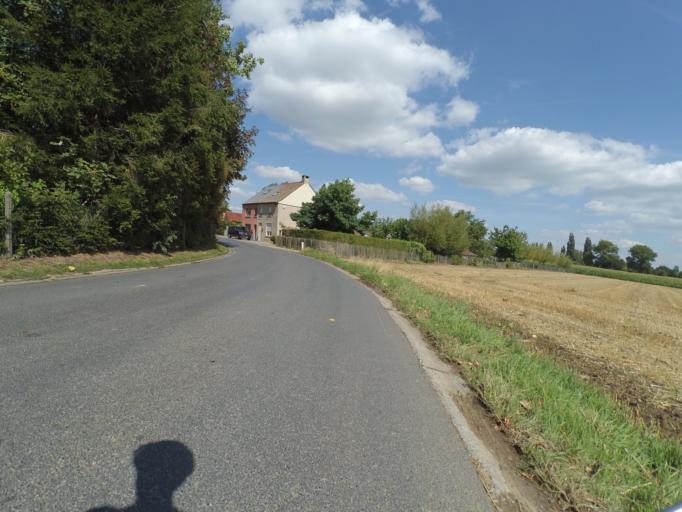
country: BE
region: Wallonia
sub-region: Province du Hainaut
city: Flobecq
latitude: 50.8102
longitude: 3.7311
